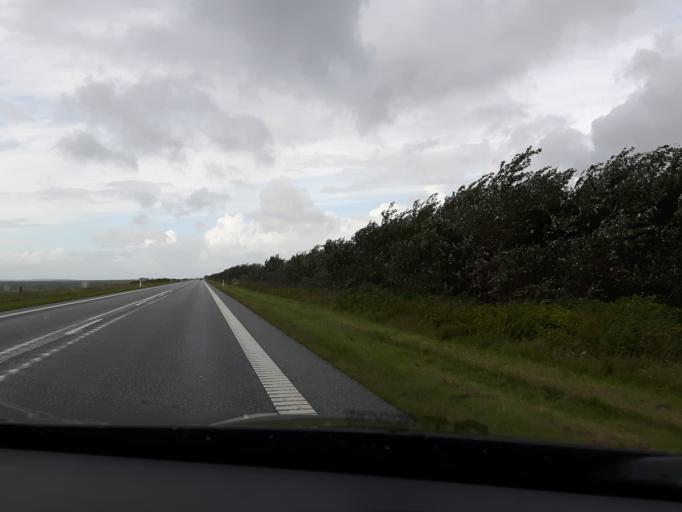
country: DK
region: North Denmark
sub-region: Jammerbugt Kommune
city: Fjerritslev
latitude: 57.0382
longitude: 9.1231
